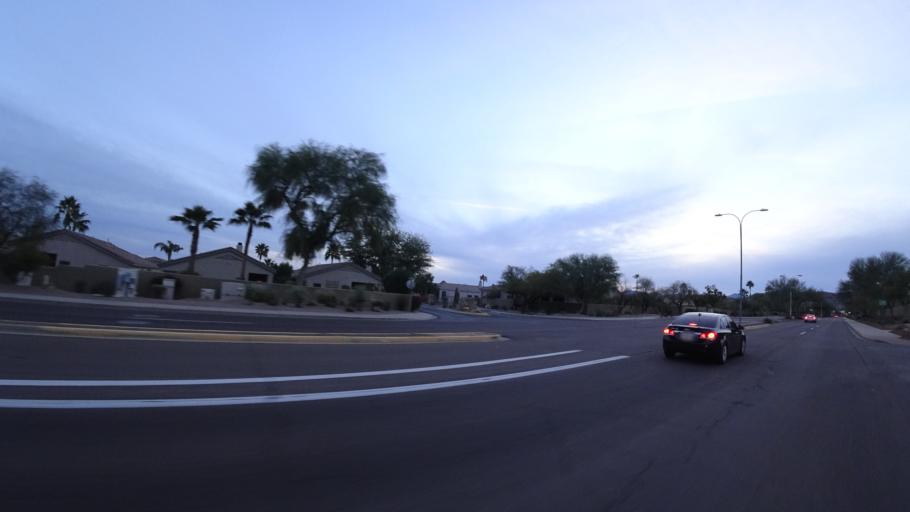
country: US
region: Arizona
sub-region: Maricopa County
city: Guadalupe
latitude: 33.3051
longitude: -112.0174
